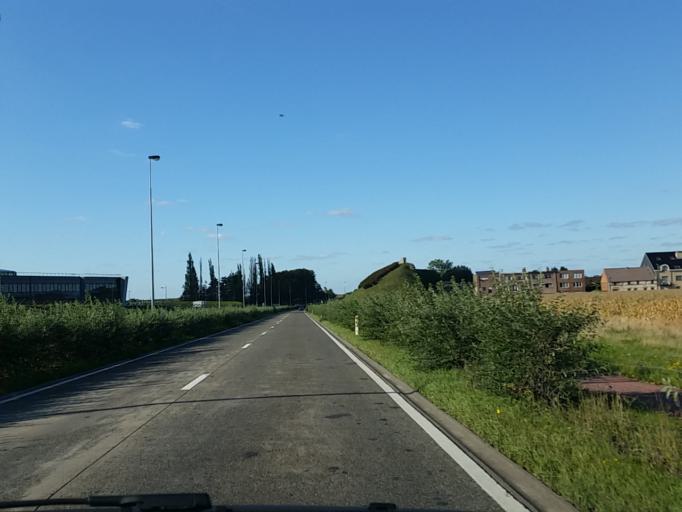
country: BE
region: Flanders
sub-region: Provincie Vlaams-Brabant
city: Steenokkerzeel
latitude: 50.9068
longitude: 4.5106
